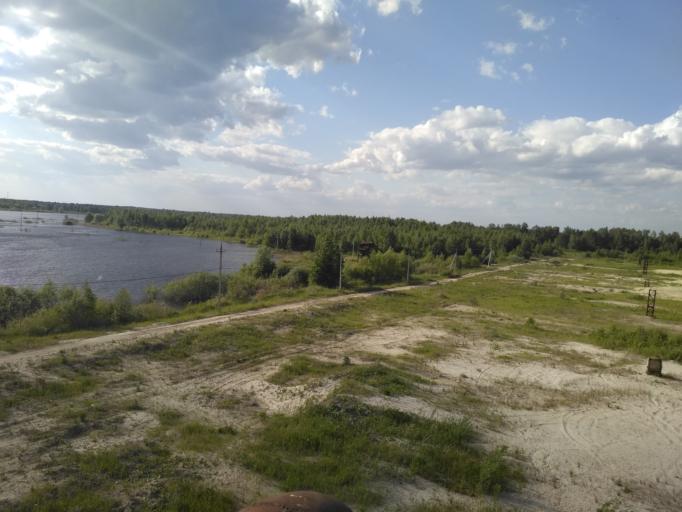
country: RU
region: Moskovskaya
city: Vereya
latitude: 55.7512
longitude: 39.1597
